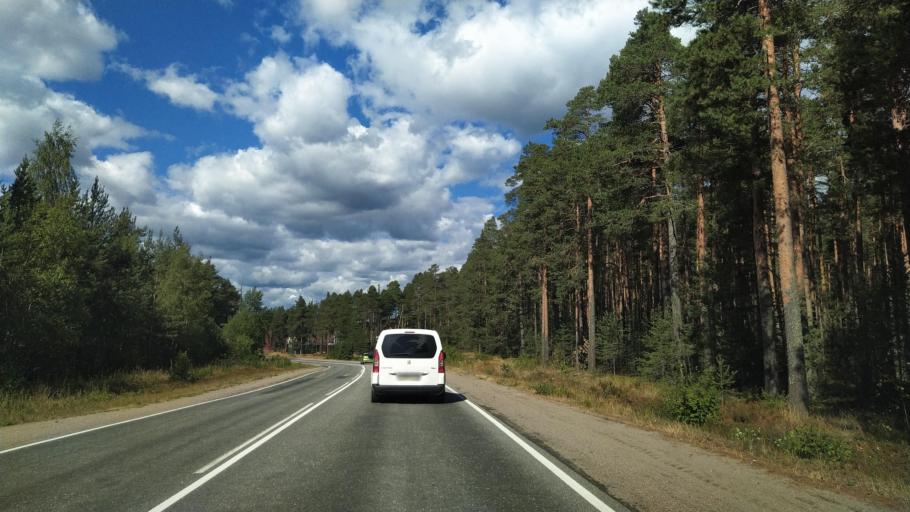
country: RU
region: Leningrad
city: Priozersk
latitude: 61.0034
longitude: 30.1906
